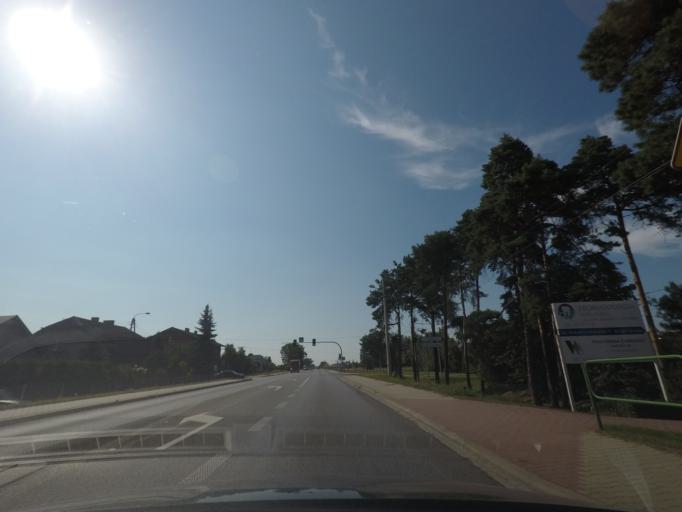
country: PL
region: Silesian Voivodeship
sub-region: Powiat pszczynski
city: Suszec
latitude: 50.0309
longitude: 18.7855
